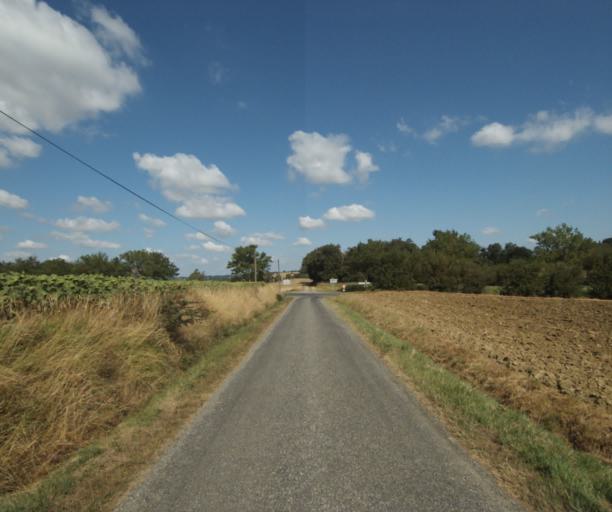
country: FR
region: Midi-Pyrenees
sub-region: Departement de la Haute-Garonne
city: Avignonet-Lauragais
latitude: 43.4432
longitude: 1.7892
